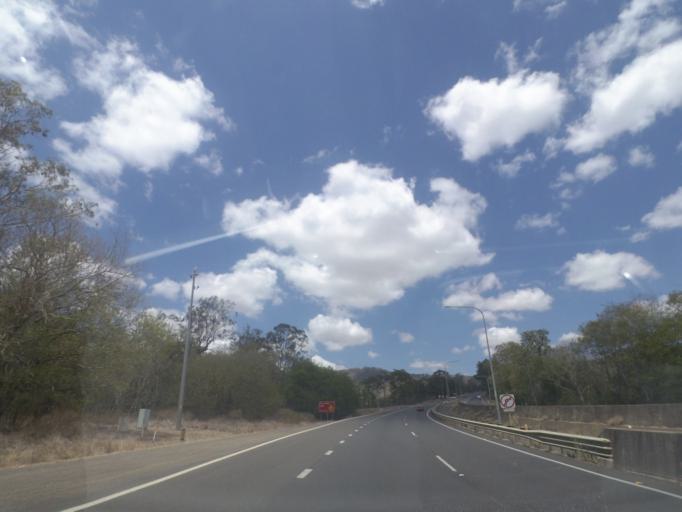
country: AU
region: Queensland
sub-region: Toowoomba
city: East Toowoomba
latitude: -27.5619
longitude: 152.0053
